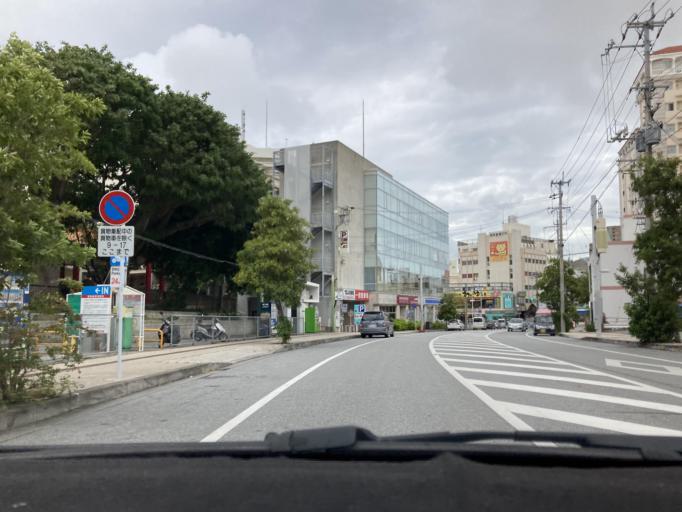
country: JP
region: Okinawa
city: Naha-shi
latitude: 26.2156
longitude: 127.6899
